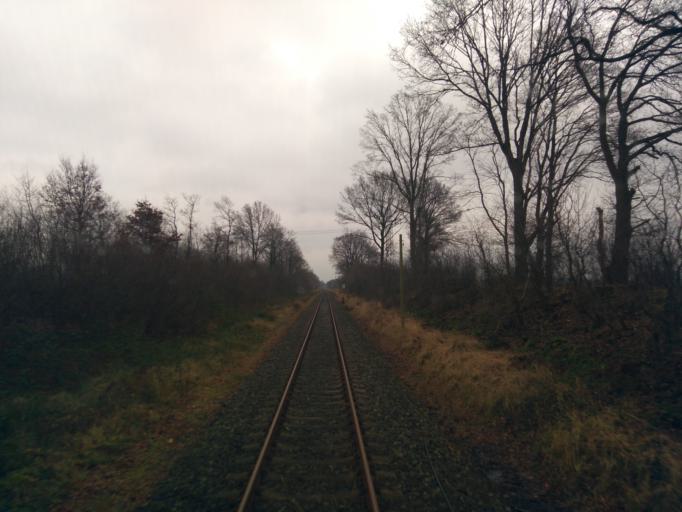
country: DE
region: Lower Saxony
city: Kirchlinteln
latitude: 52.9539
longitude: 9.2938
